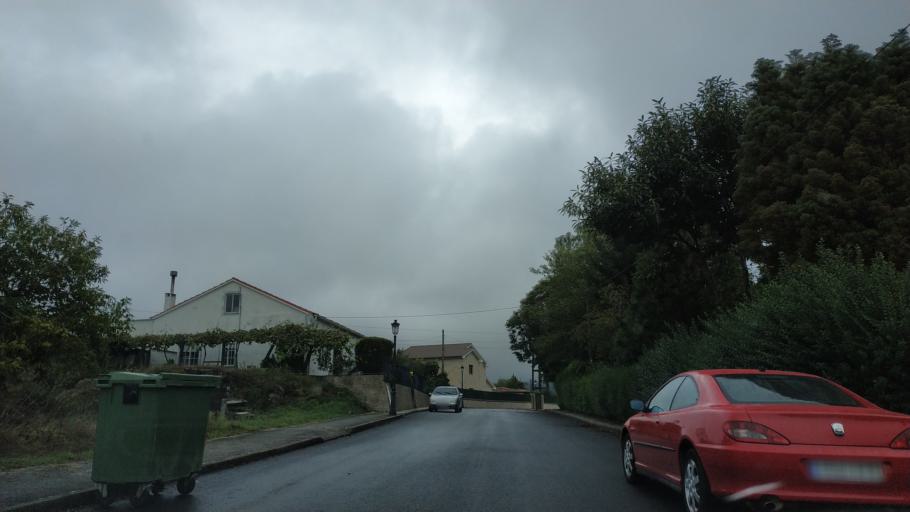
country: ES
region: Galicia
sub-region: Provincia da Coruna
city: Negreira
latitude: 42.9103
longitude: -8.7419
